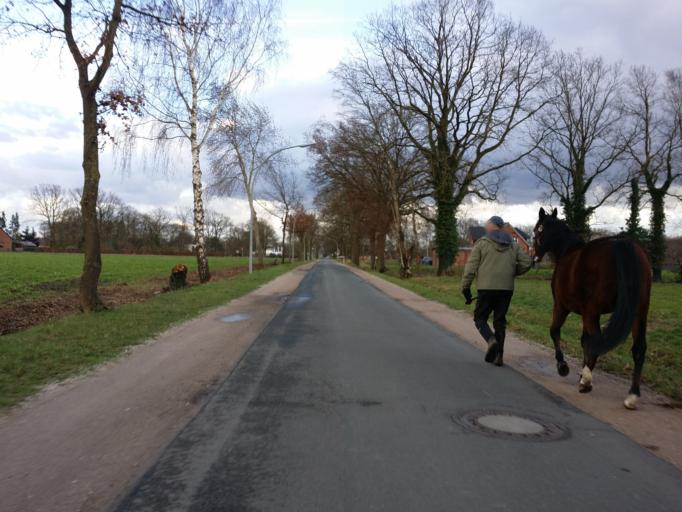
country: DE
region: Lower Saxony
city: Delmenhorst
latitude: 53.0134
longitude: 8.6407
